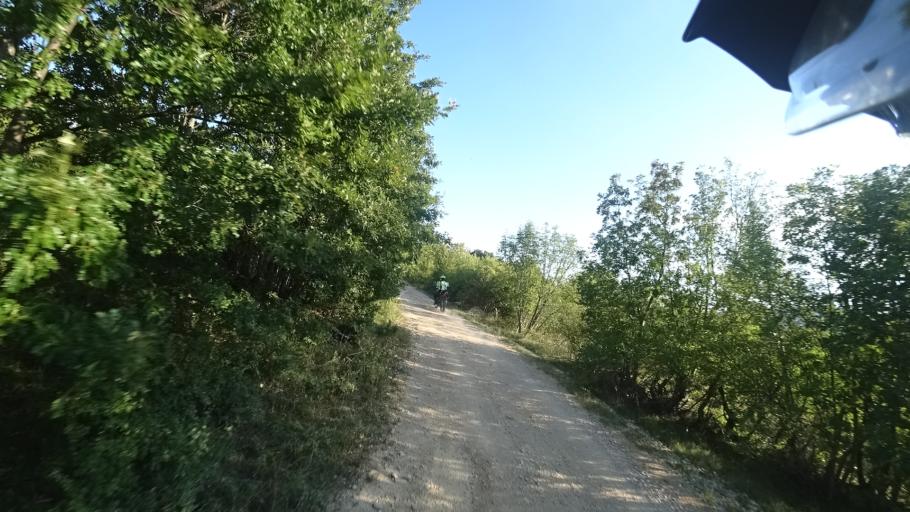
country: HR
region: Sibensko-Kniniska
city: Knin
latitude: 44.1581
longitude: 16.0922
